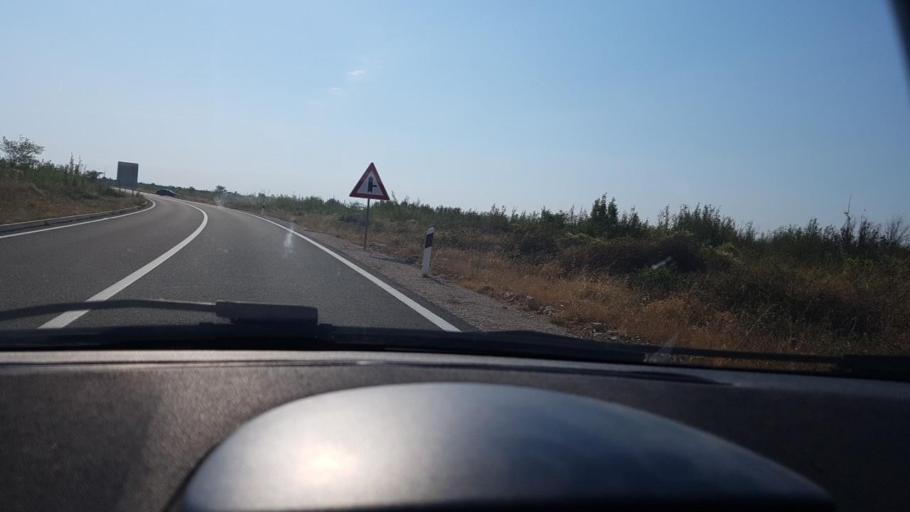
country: HR
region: Sibensko-Kniniska
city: Zaton
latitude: 43.8843
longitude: 15.7851
